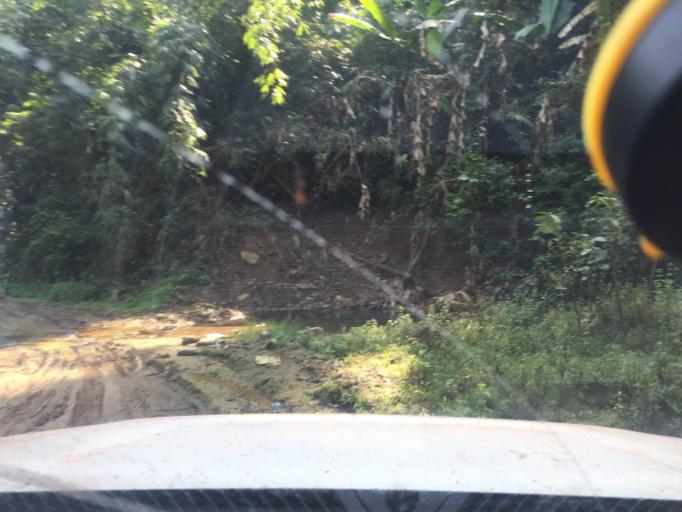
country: LA
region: Phongsali
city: Phongsali
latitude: 21.7013
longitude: 102.3918
